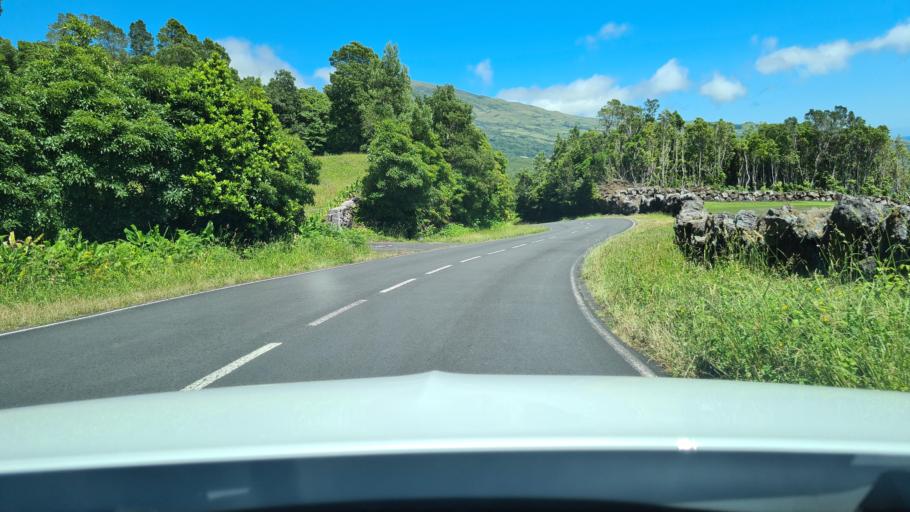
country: PT
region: Azores
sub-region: Sao Roque do Pico
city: Sao Roque do Pico
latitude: 38.4266
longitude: -28.2897
